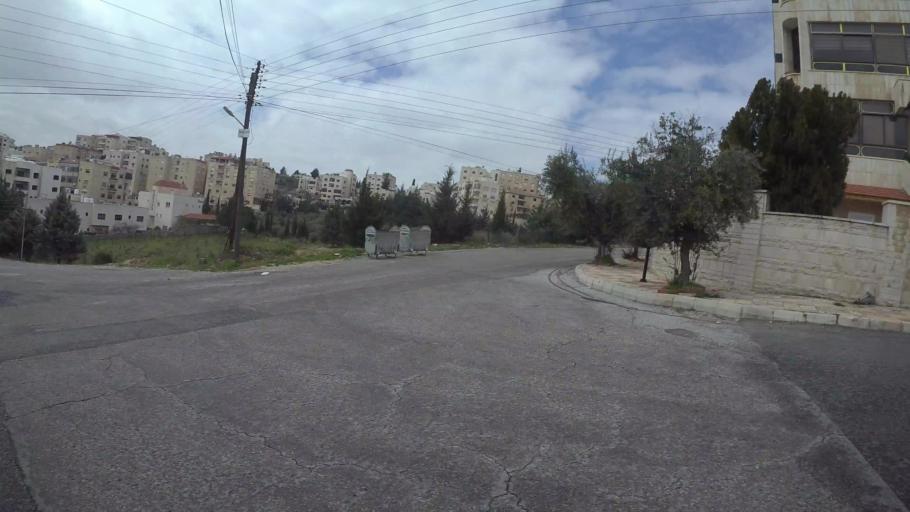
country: JO
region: Amman
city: Al Jubayhah
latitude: 31.9932
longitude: 35.8566
